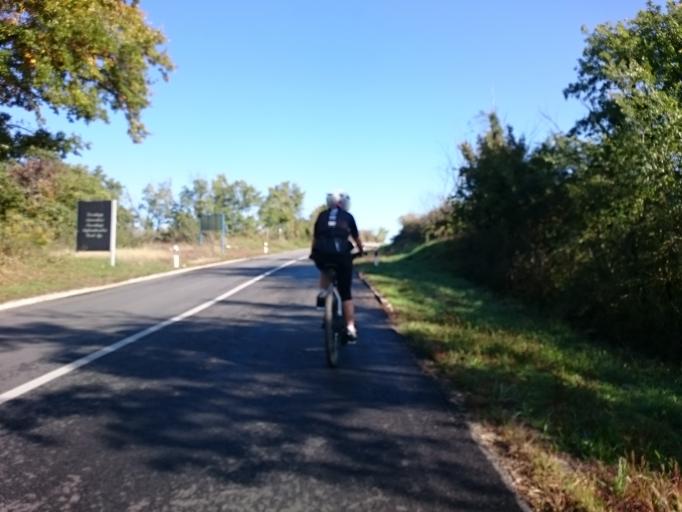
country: HR
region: Istarska
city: Buje
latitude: 45.3830
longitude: 13.6286
